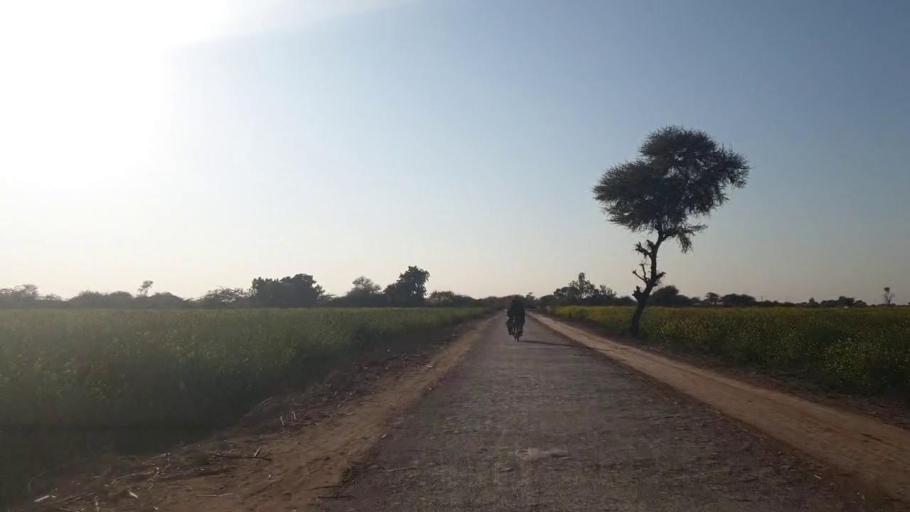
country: PK
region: Sindh
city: Khadro
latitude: 26.0591
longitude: 68.6783
